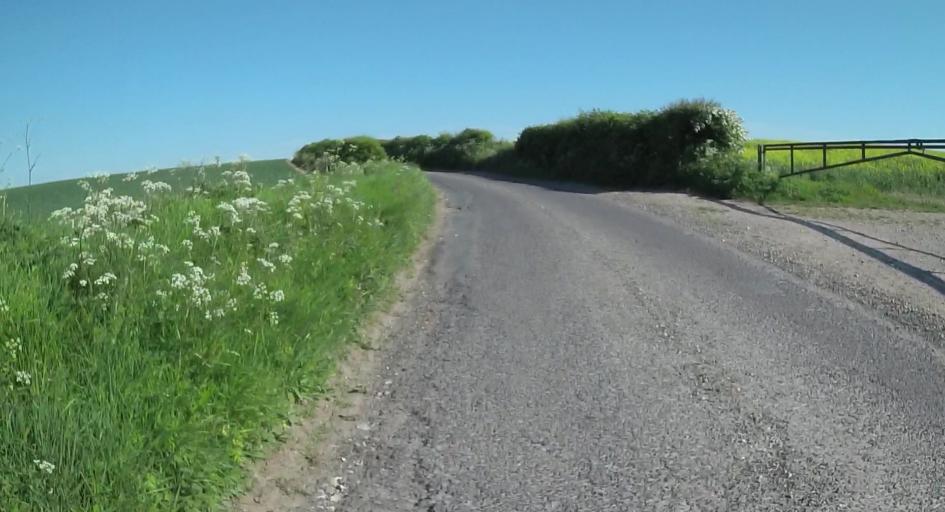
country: GB
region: England
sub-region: Hampshire
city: Overton
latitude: 51.1686
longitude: -1.1936
